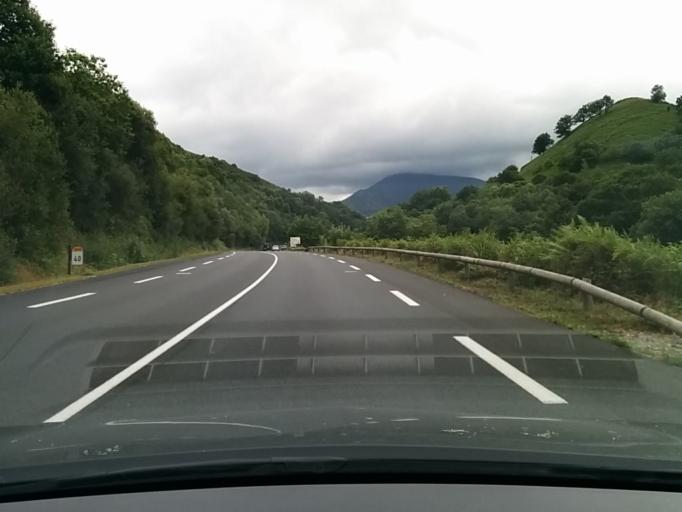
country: FR
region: Aquitaine
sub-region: Departement des Pyrenees-Atlantiques
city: Itxassou
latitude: 43.3003
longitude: -1.3500
